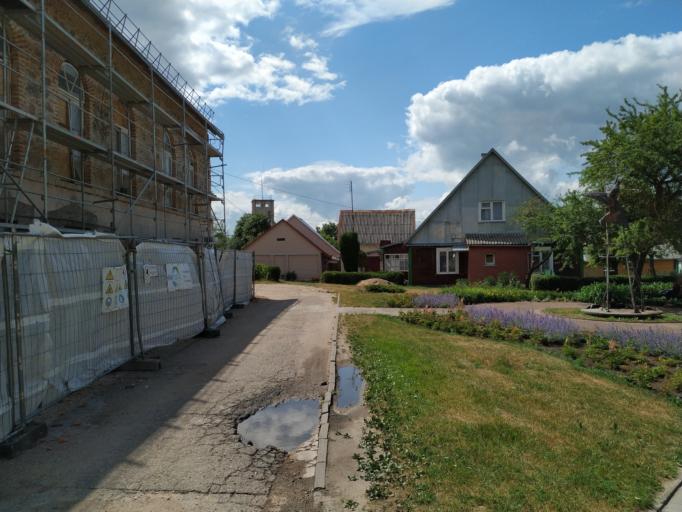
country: LT
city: Kupiskis
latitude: 55.8399
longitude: 24.9758
